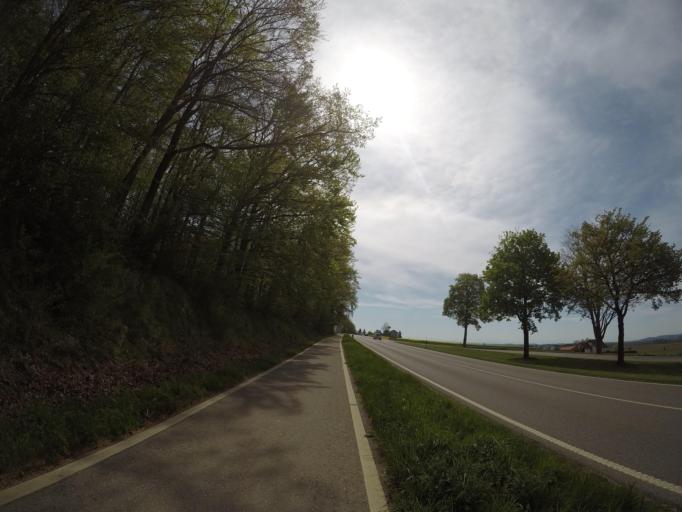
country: DE
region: Baden-Wuerttemberg
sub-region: Tuebingen Region
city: Boms
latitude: 47.9546
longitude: 9.5186
